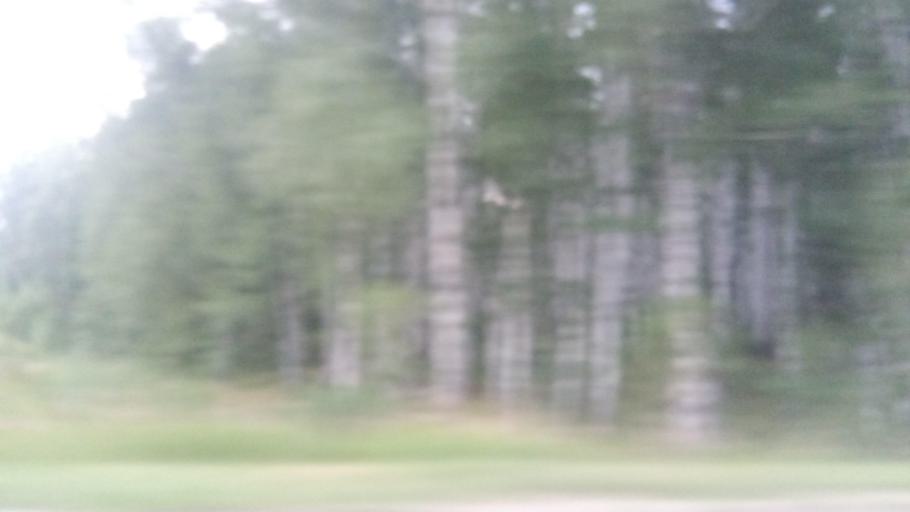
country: RU
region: Chelyabinsk
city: Sargazy
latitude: 54.9712
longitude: 61.2211
